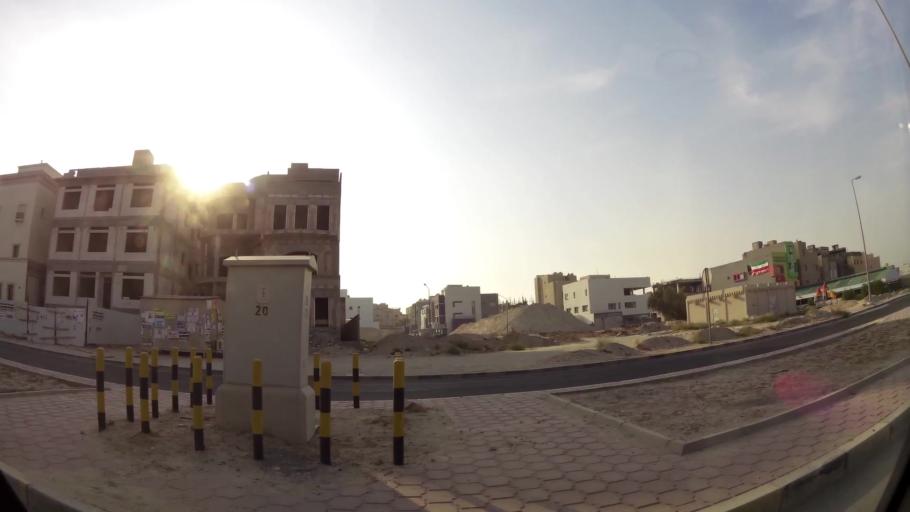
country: KW
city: Al Funaytis
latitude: 29.2303
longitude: 48.0900
